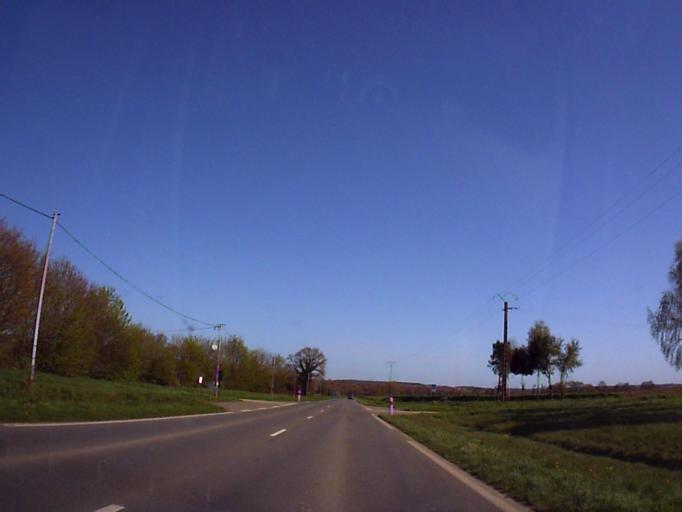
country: FR
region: Brittany
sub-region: Departement d'Ille-et-Vilaine
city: Quedillac
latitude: 48.2349
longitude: -2.1727
